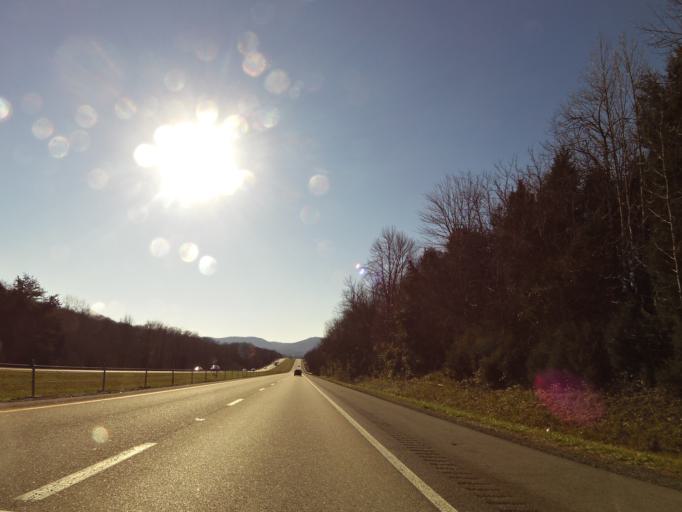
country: US
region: Tennessee
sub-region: Jefferson County
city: White Pine
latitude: 36.0155
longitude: -83.2957
